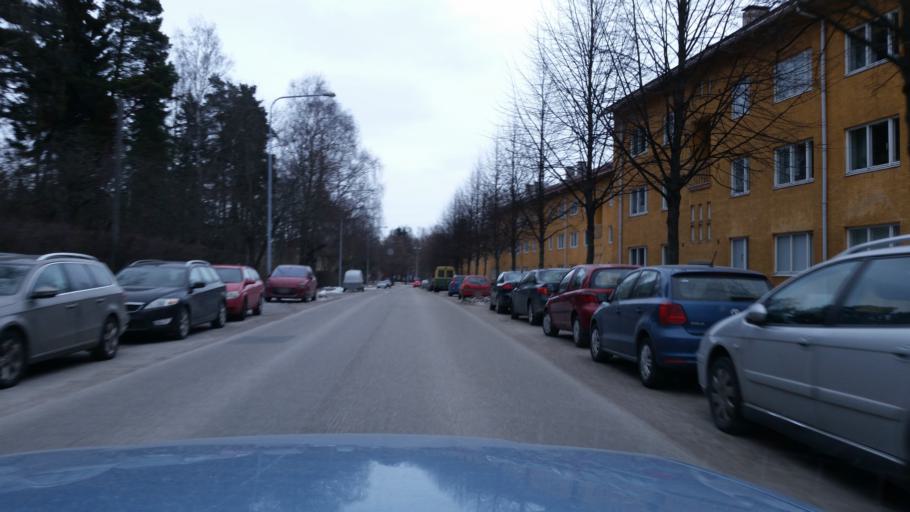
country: FI
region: Uusimaa
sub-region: Helsinki
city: Helsinki
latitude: 60.2180
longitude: 24.9573
